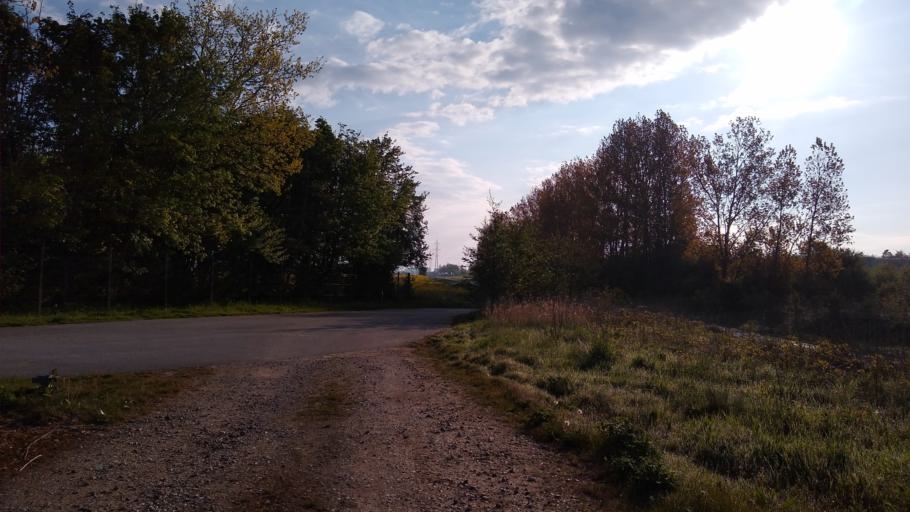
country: DK
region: South Denmark
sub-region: Fredericia Kommune
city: Fredericia
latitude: 55.5893
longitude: 9.7125
